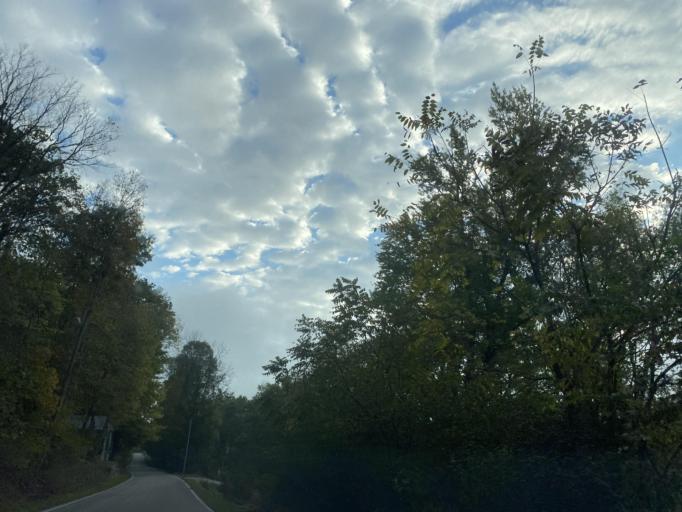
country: US
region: Kentucky
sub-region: Pendleton County
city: Falmouth
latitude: 38.7491
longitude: -84.3354
